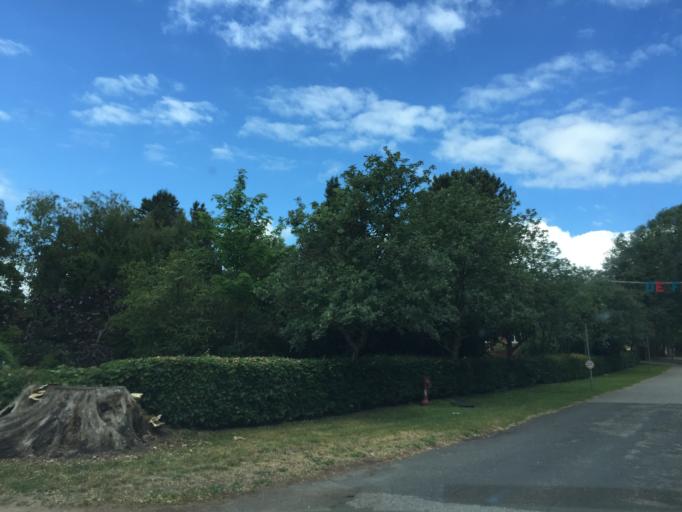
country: DK
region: South Denmark
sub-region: Svendborg Kommune
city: Svendborg
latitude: 55.0716
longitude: 10.5151
